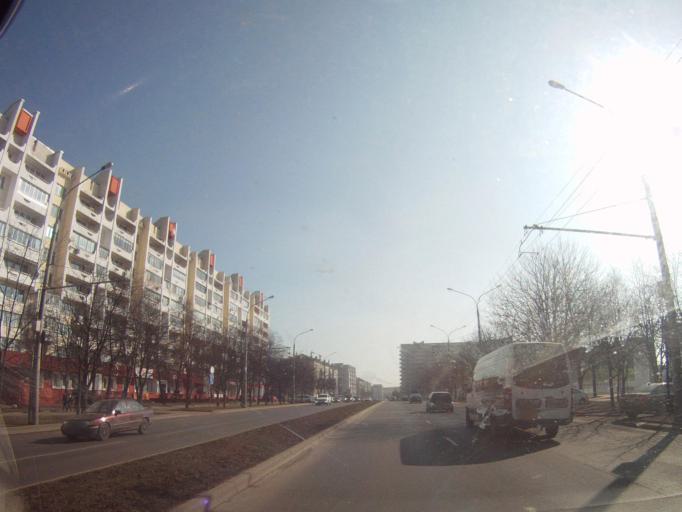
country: BY
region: Minsk
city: Minsk
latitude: 53.9272
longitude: 27.5904
